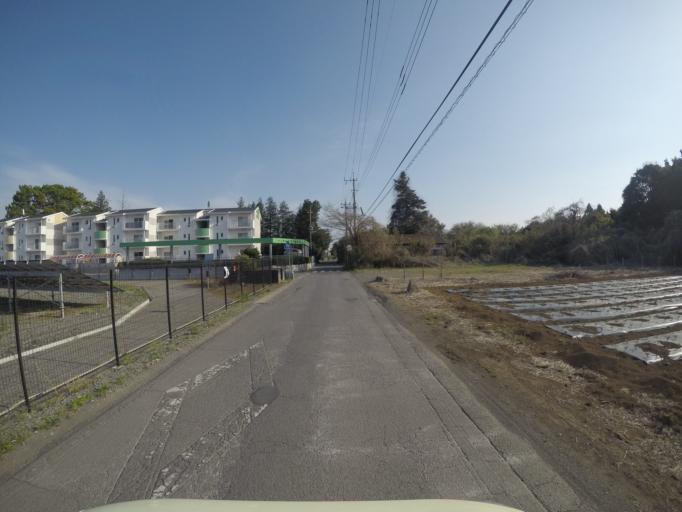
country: JP
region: Ibaraki
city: Ishige
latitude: 36.1561
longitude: 140.0164
